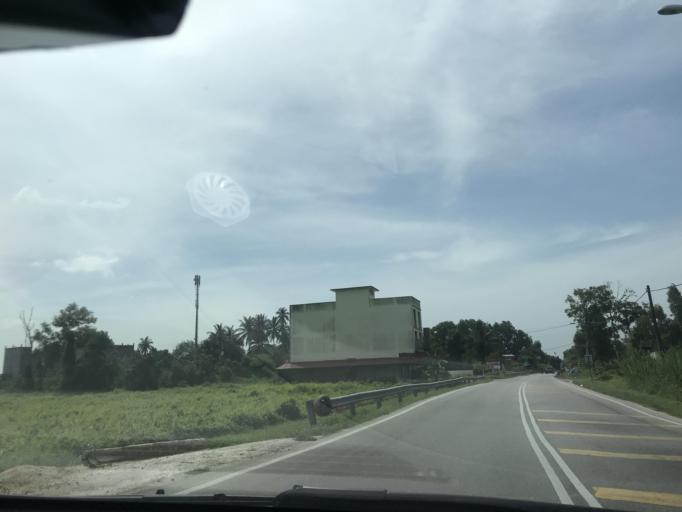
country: MY
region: Kelantan
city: Tumpat
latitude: 6.1878
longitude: 102.1612
